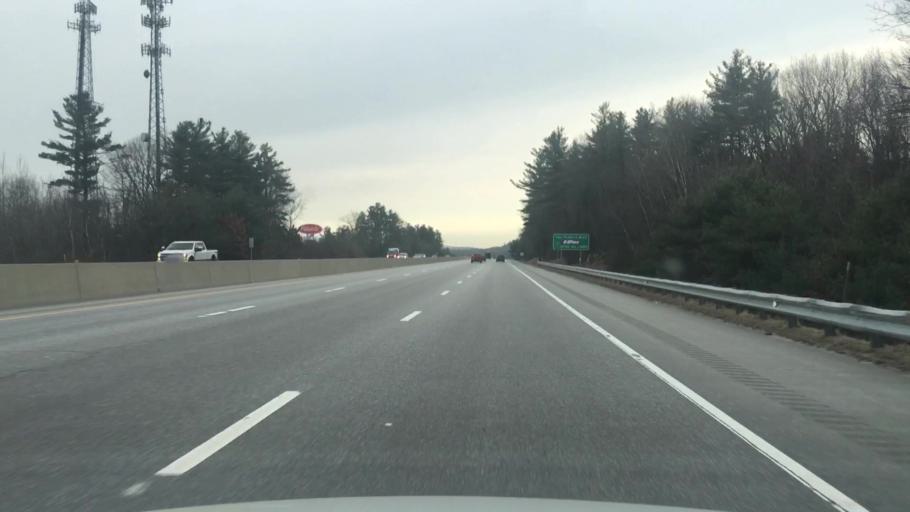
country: US
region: New Hampshire
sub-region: Merrimack County
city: Bow Bog
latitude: 43.1217
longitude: -71.4827
